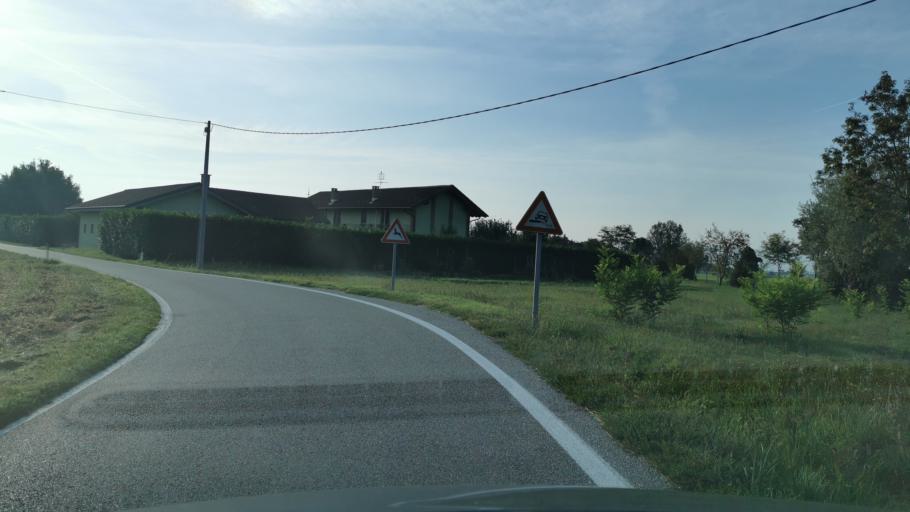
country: IT
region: Piedmont
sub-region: Provincia di Torino
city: Borgaro Torinese
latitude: 45.1629
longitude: 7.6717
